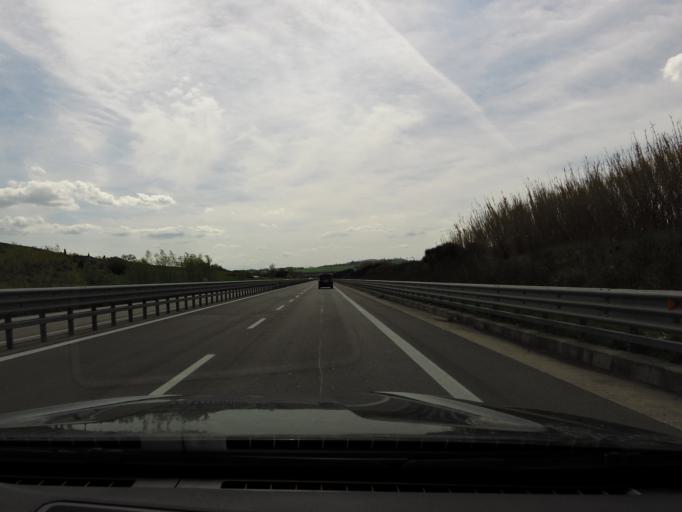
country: IT
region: The Marches
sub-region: Provincia di Ancona
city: San Biagio
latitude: 43.5501
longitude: 13.5167
